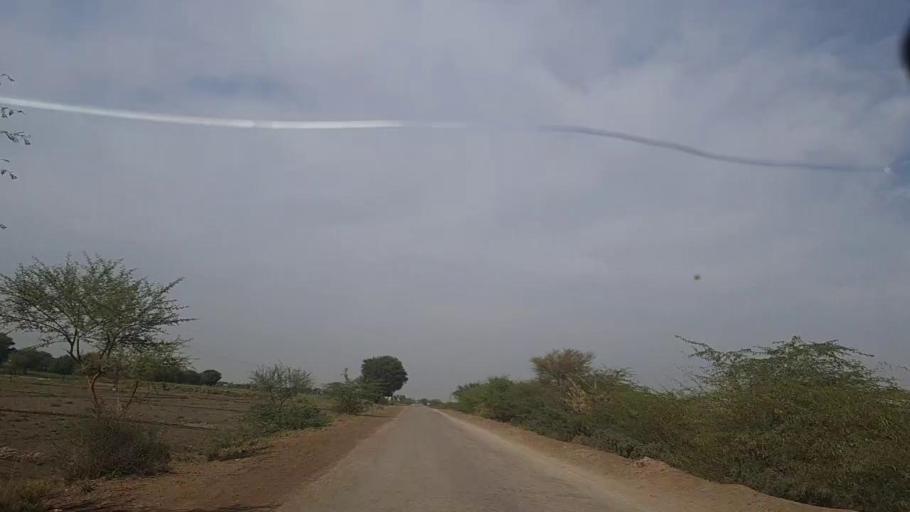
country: PK
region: Sindh
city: Pithoro
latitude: 25.5576
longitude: 69.3628
